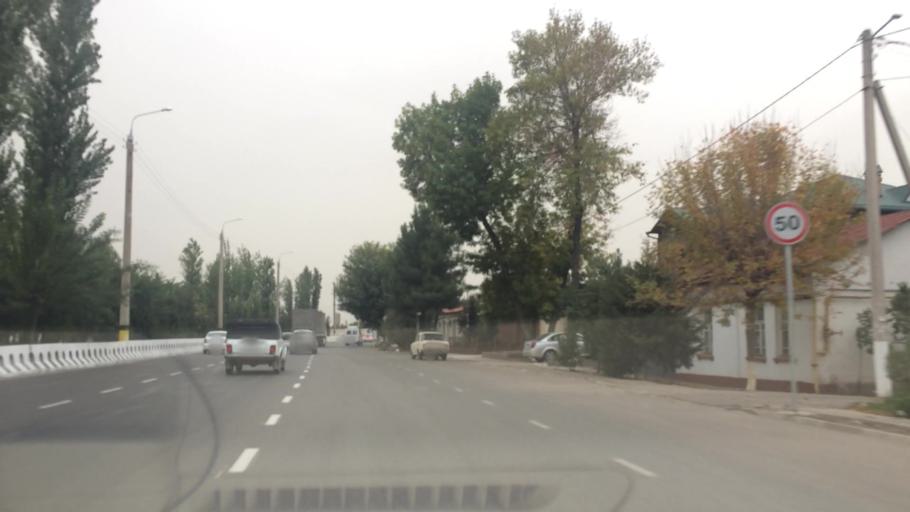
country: UZ
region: Toshkent
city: Salor
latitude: 41.3082
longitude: 69.3422
